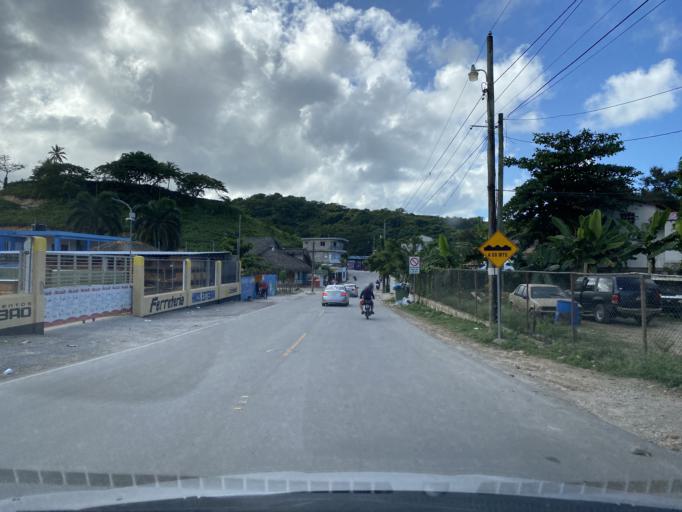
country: DO
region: Samana
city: Las Terrenas
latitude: 19.3042
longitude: -69.5473
